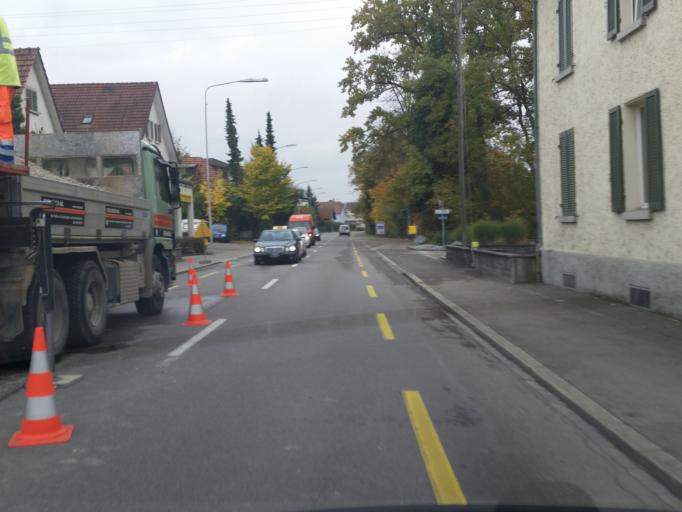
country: CH
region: Zurich
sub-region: Bezirk Dietikon
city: Geroldswil
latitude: 47.4125
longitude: 8.4142
